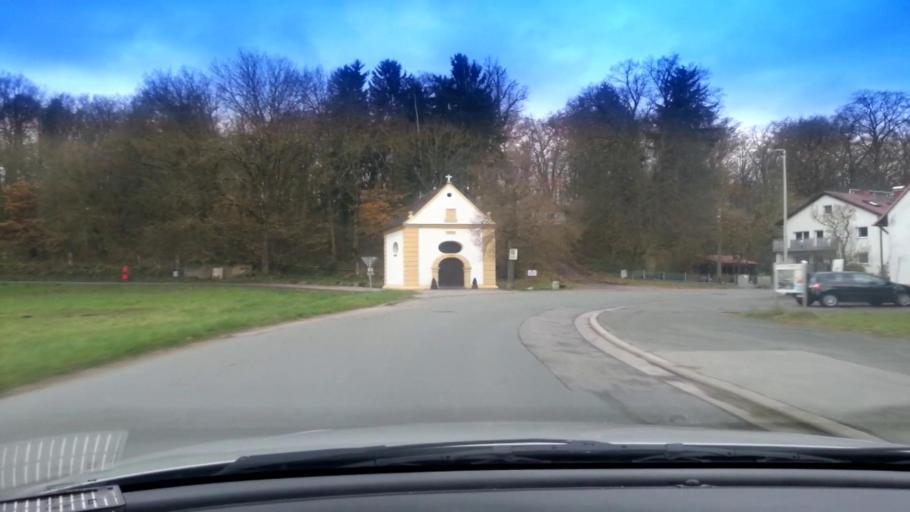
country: DE
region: Bavaria
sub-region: Upper Franconia
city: Stegaurach
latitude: 49.8610
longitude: 10.8411
